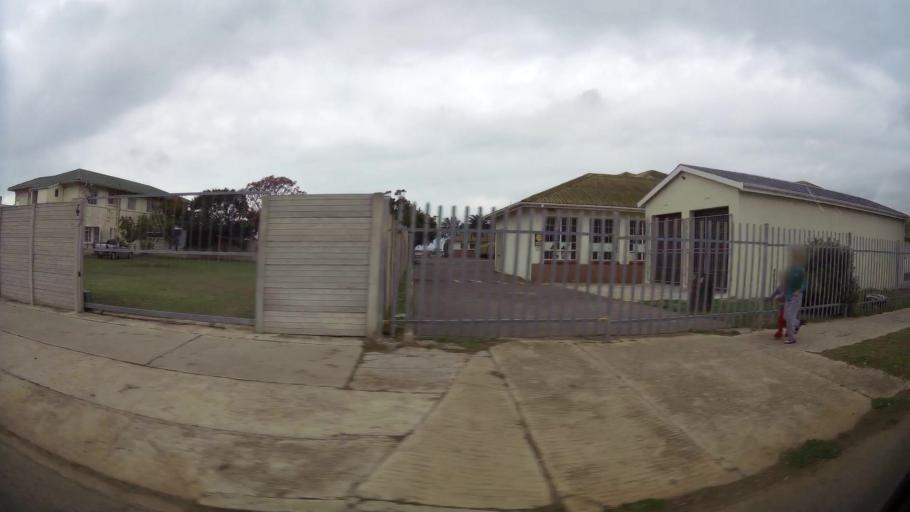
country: ZA
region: Eastern Cape
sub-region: Nelson Mandela Bay Metropolitan Municipality
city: Port Elizabeth
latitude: -33.9055
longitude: 25.5666
